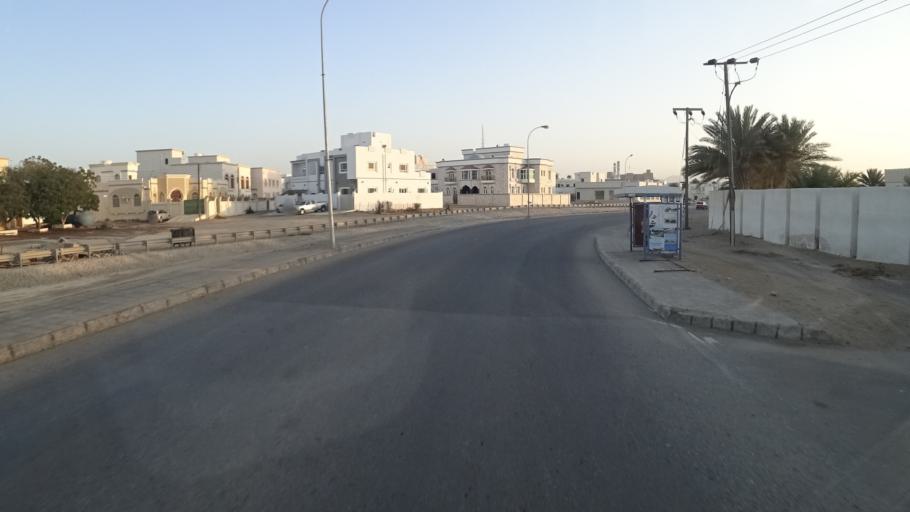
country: OM
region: Ash Sharqiyah
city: Sur
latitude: 22.5845
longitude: 59.5057
